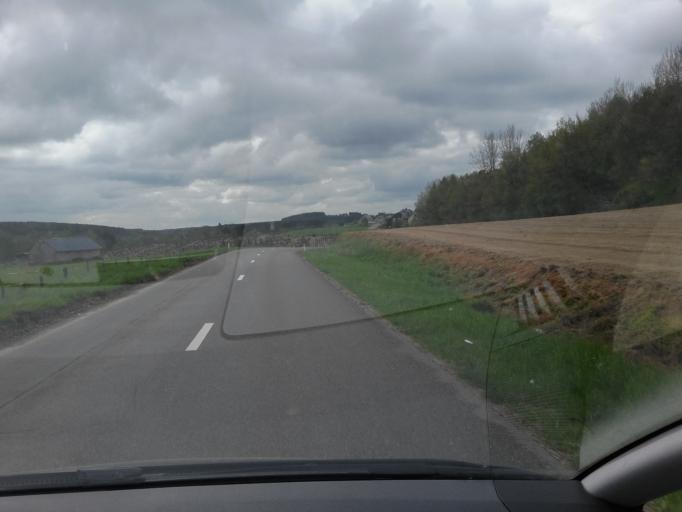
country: BE
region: Wallonia
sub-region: Province du Luxembourg
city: Bertrix
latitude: 49.8283
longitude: 5.3173
